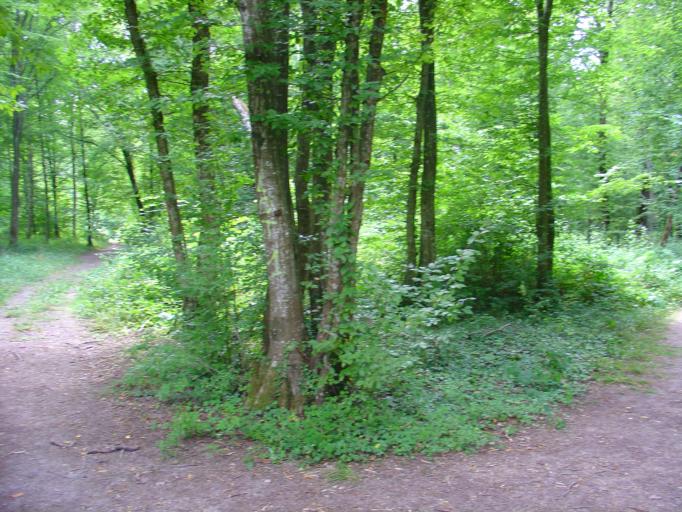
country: FR
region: Lorraine
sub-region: Departement de la Meuse
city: Dieue-sur-Meuse
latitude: 48.9247
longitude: 5.3937
